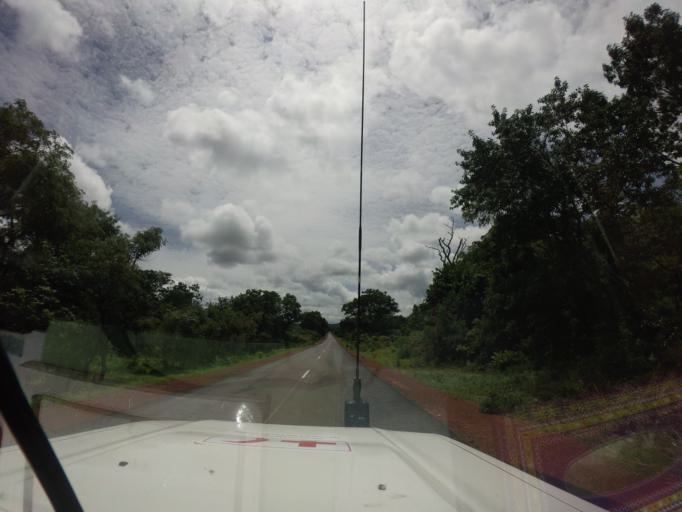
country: SL
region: Northern Province
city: Gberia Fotombu
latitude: 10.1213
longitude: -11.1586
